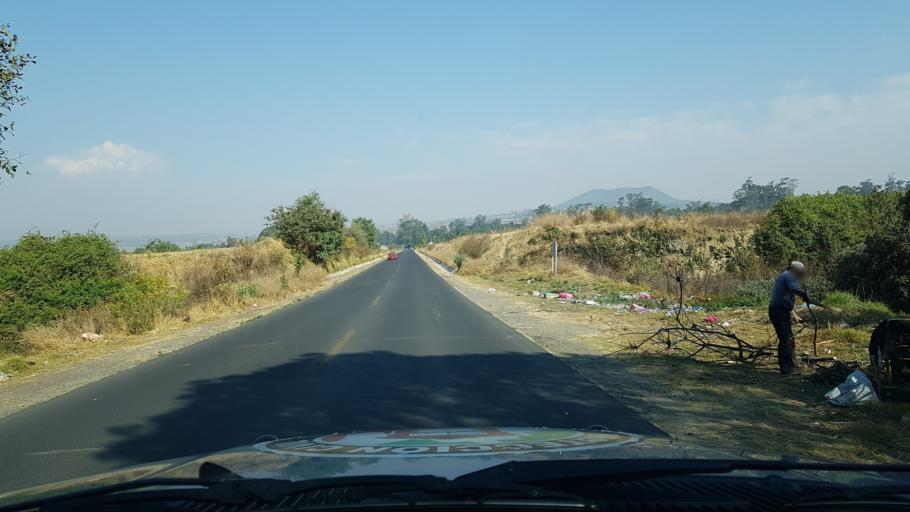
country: MX
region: Mexico
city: Ozumba de Alzate
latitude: 19.0473
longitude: -98.7774
